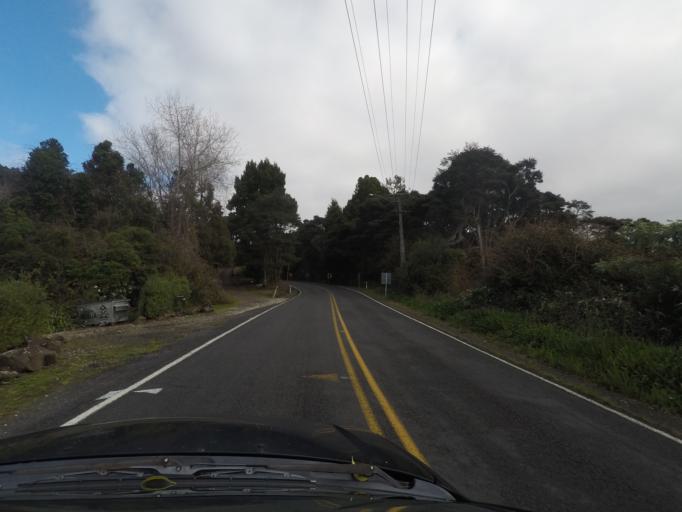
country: NZ
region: Auckland
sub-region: Auckland
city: Muriwai Beach
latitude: -36.8779
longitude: 174.5442
